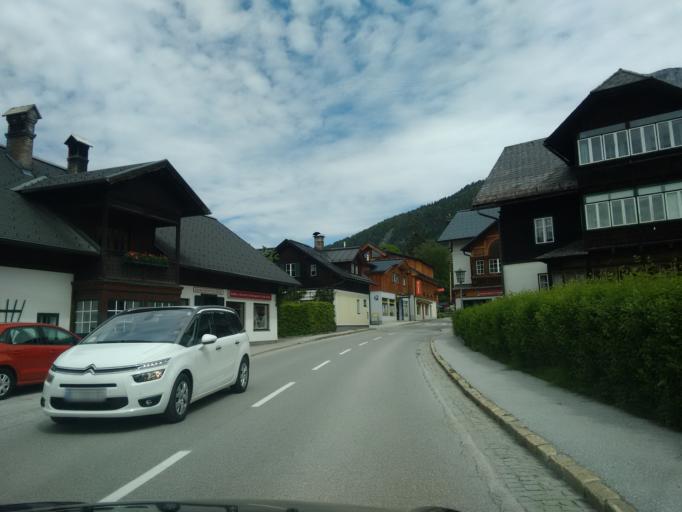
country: AT
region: Styria
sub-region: Politischer Bezirk Liezen
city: Altaussee
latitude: 47.6370
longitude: 13.7626
